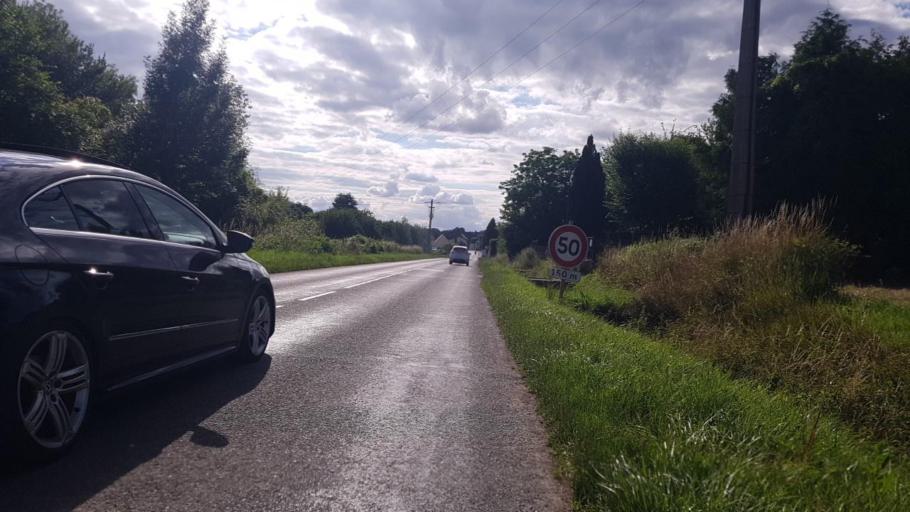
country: FR
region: Picardie
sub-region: Departement de l'Aisne
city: Brasles
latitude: 49.0468
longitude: 3.4363
